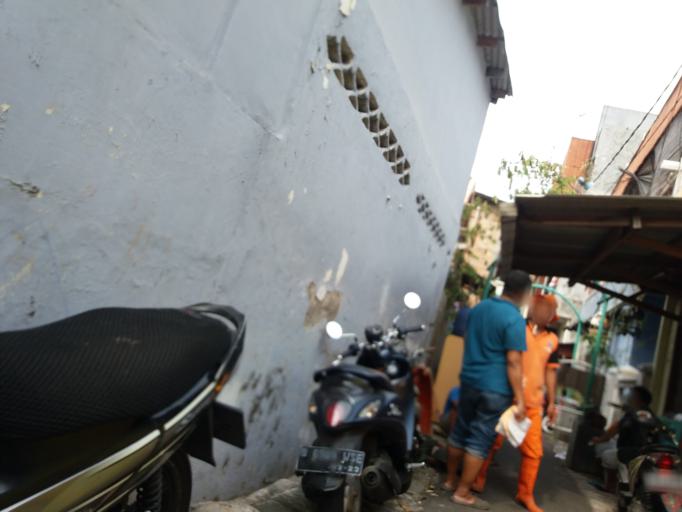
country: ID
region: Jakarta Raya
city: Jakarta
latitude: -6.1855
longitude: 106.8281
